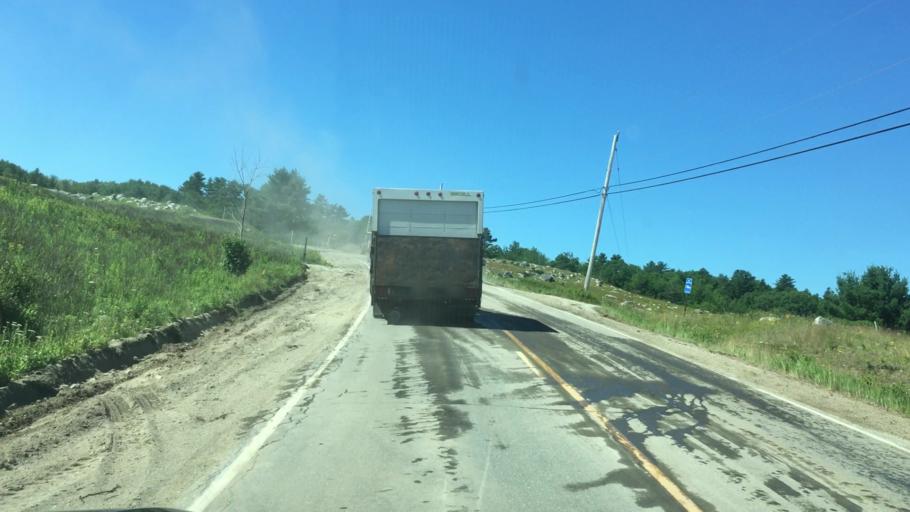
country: US
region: Maine
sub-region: Hancock County
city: Sedgwick
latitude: 44.3541
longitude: -68.5852
